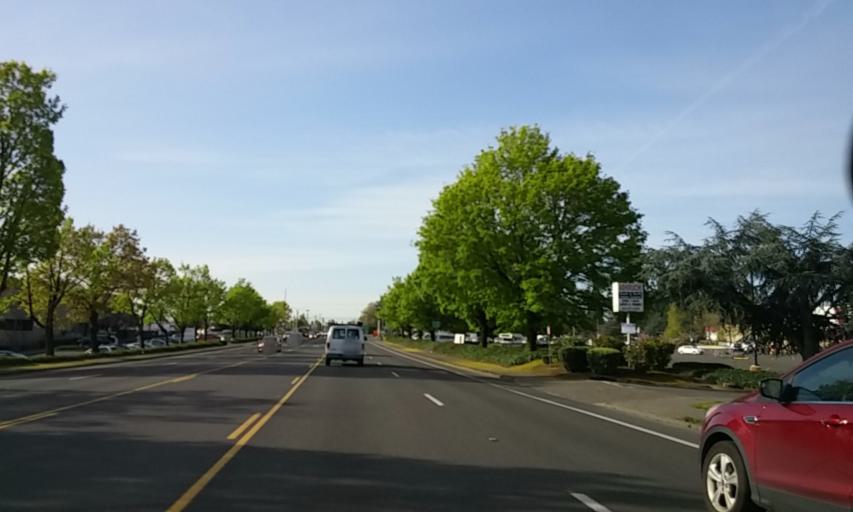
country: US
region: Oregon
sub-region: Washington County
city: Beaverton
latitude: 45.4925
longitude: -122.8262
